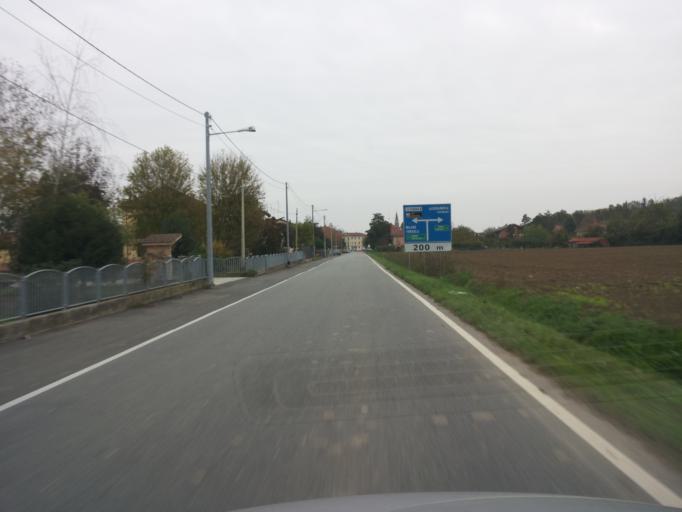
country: IT
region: Piedmont
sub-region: Provincia di Alessandria
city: Terruggia
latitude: 45.1019
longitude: 8.4488
